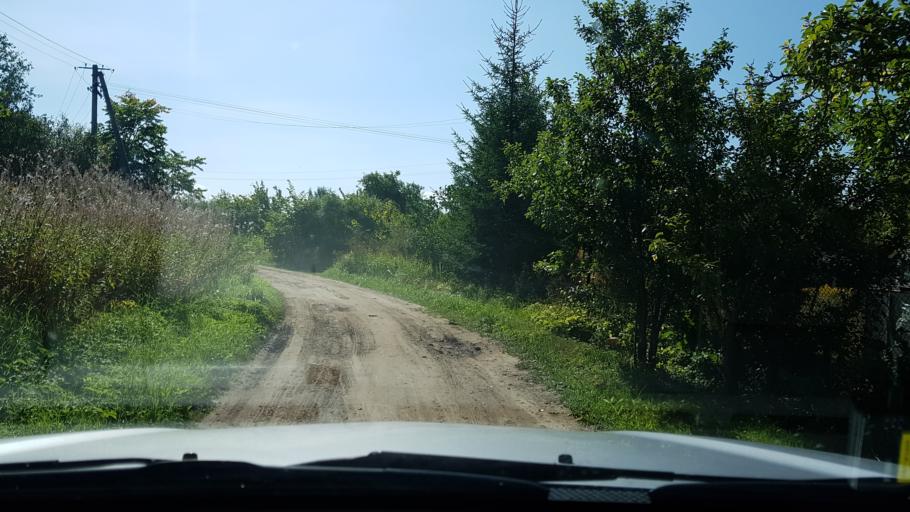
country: EE
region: Ida-Virumaa
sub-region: Sillamaee linn
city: Sillamae
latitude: 59.3252
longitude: 27.7760
